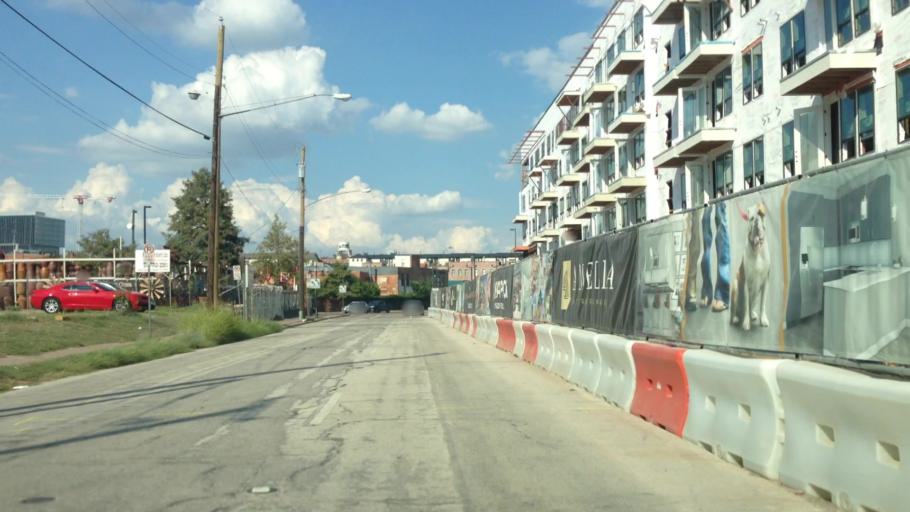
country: US
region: Texas
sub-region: Dallas County
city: Dallas
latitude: 32.7771
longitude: -96.7922
